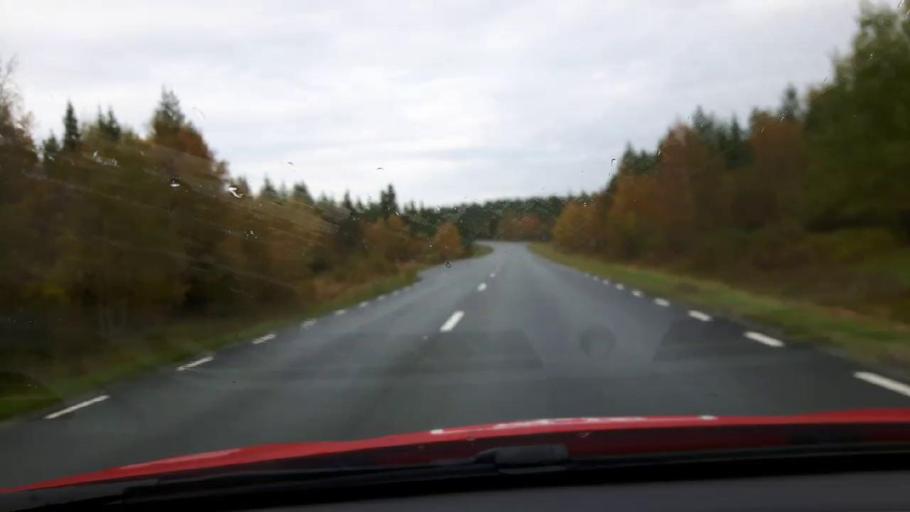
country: SE
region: Jaemtland
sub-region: Krokoms Kommun
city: Krokom
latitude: 63.0910
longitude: 14.3004
